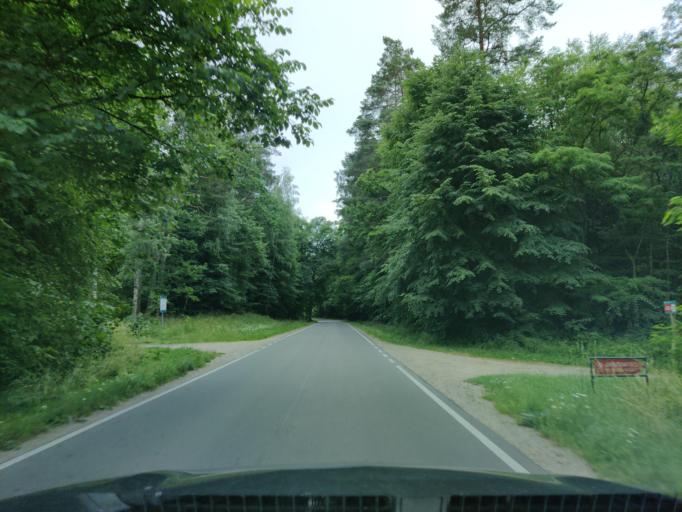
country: PL
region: Warmian-Masurian Voivodeship
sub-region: Powiat gizycki
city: Ryn
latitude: 53.8838
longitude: 21.5785
